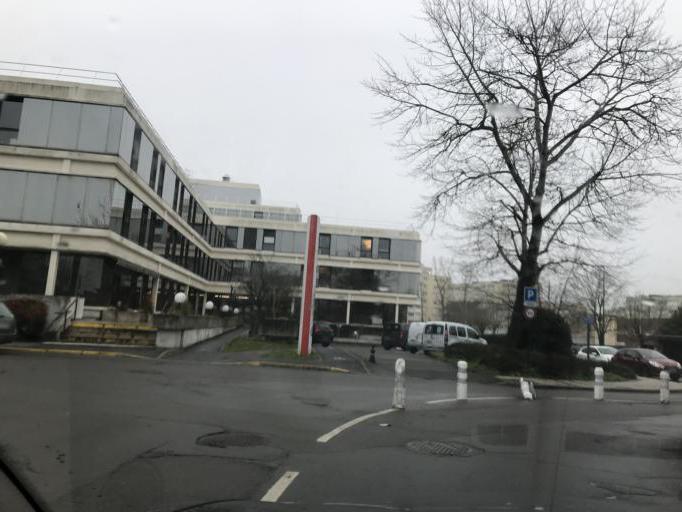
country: FR
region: Ile-de-France
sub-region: Departement du Val-d'Oise
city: Cergy-Pontoise
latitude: 49.0339
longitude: 2.0876
